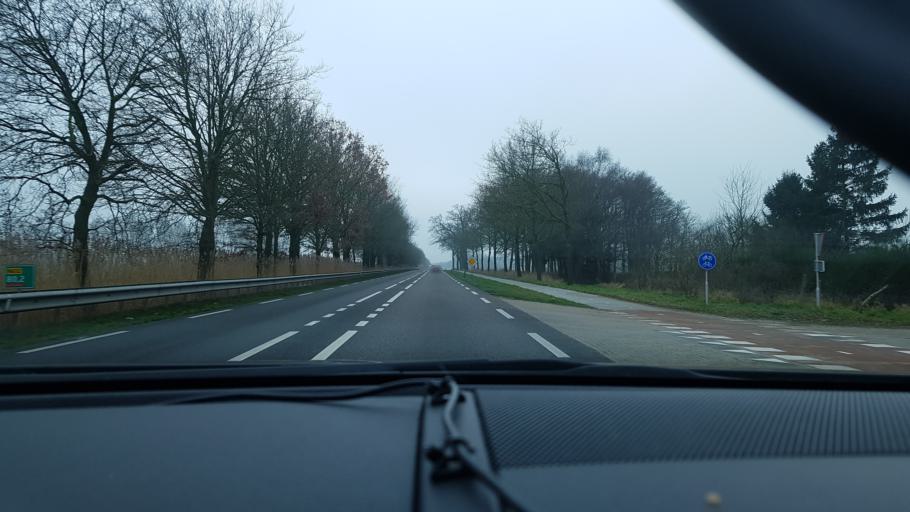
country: NL
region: North Brabant
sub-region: Gemeente Someren
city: Someren
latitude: 51.4341
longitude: 5.6949
